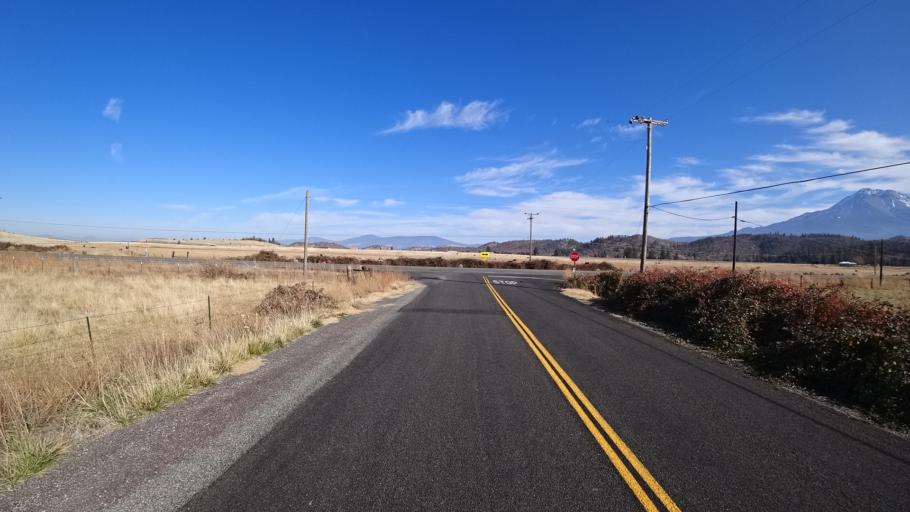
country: US
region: California
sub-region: Siskiyou County
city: Weed
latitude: 41.4439
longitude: -122.4428
